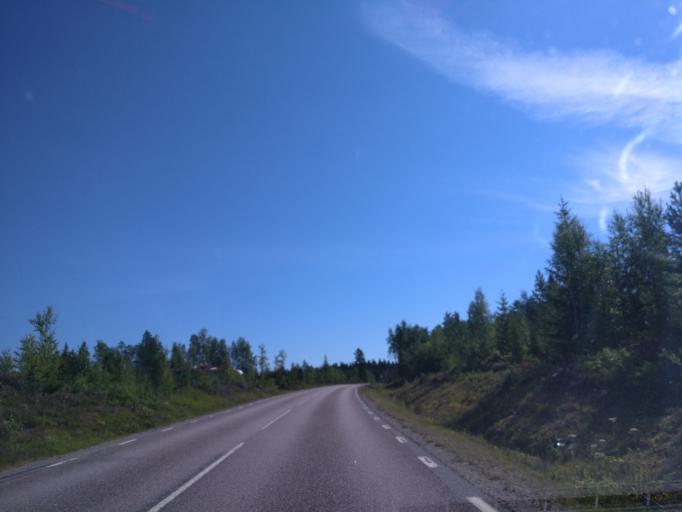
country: SE
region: Vaermland
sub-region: Filipstads Kommun
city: Lesjofors
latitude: 60.0469
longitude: 13.9855
